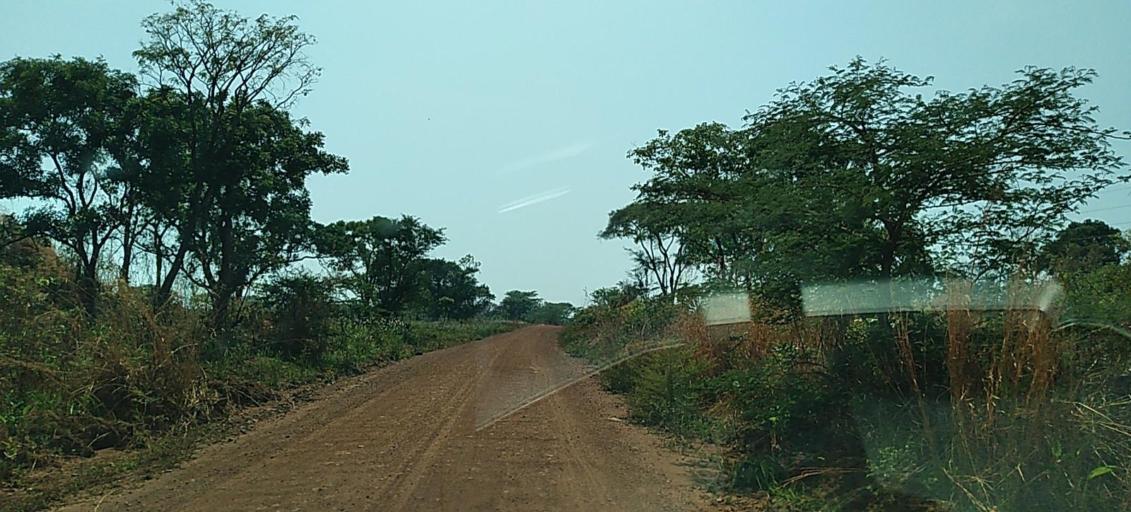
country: ZM
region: North-Western
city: Kansanshi
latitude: -12.0054
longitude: 26.5353
